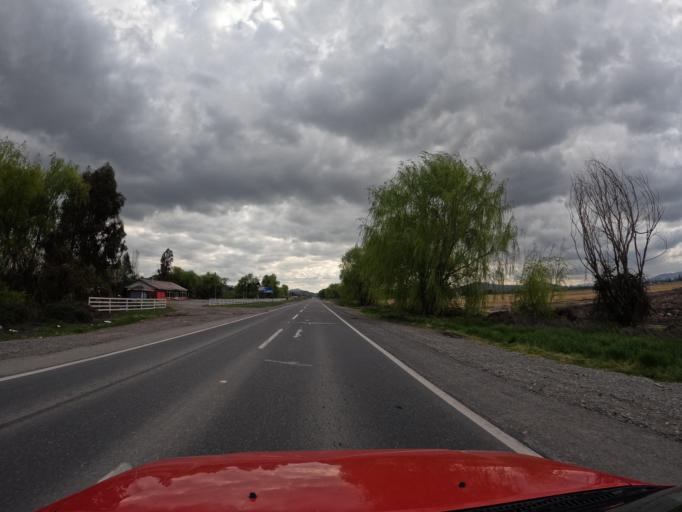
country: CL
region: Maule
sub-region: Provincia de Linares
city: San Javier
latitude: -35.6306
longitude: -71.7222
